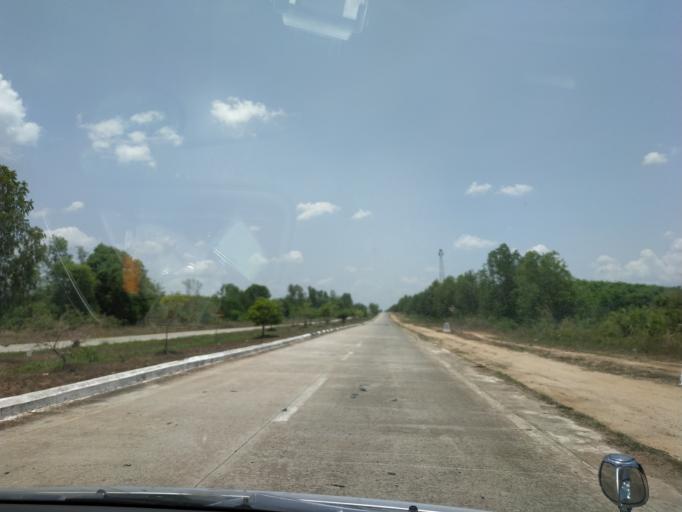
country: MM
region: Bago
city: Thanatpin
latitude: 17.3853
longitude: 96.3110
